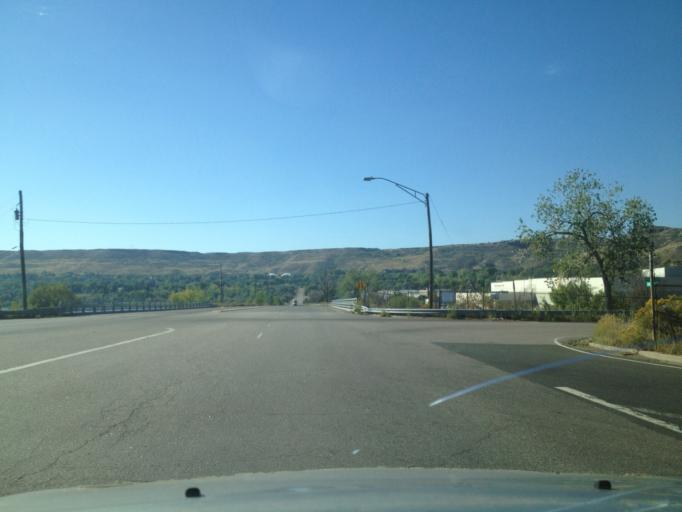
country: US
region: Colorado
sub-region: Jefferson County
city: Applewood
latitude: 39.7724
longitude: -105.1749
